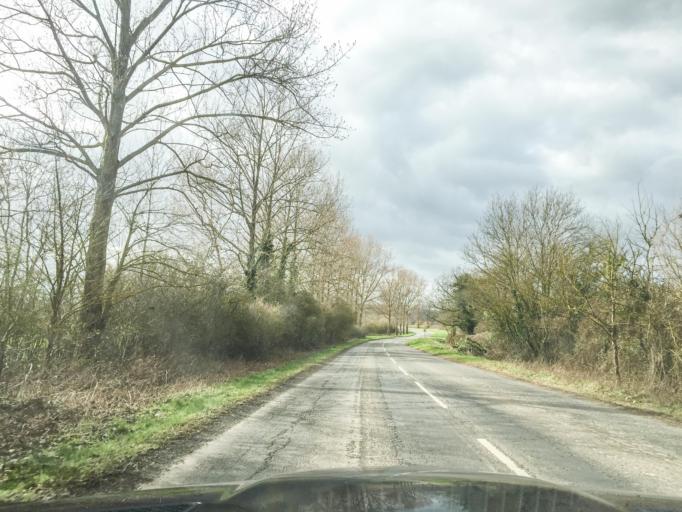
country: GB
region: England
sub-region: Warwickshire
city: Shipston on Stour
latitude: 52.0617
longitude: -1.5741
